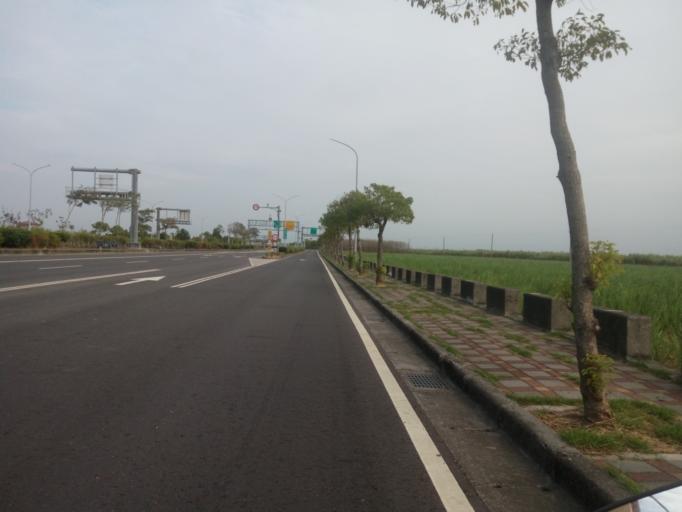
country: TW
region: Taiwan
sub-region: Chiayi
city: Taibao
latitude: 23.4828
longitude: 120.3668
